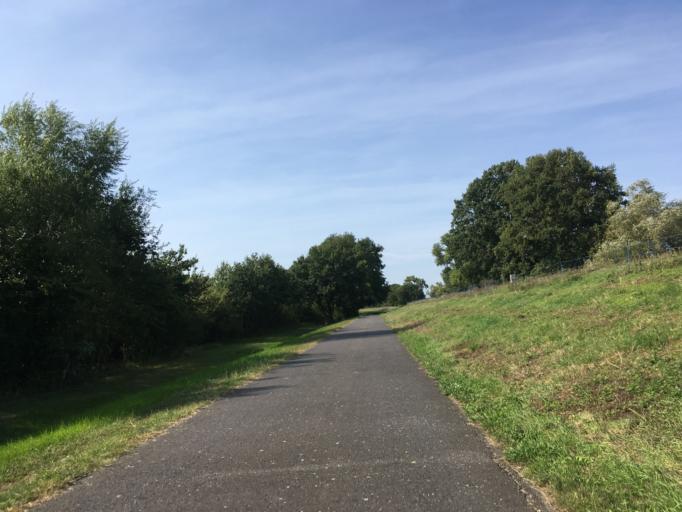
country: DE
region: Brandenburg
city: Vogelsang
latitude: 52.2457
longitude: 14.6960
